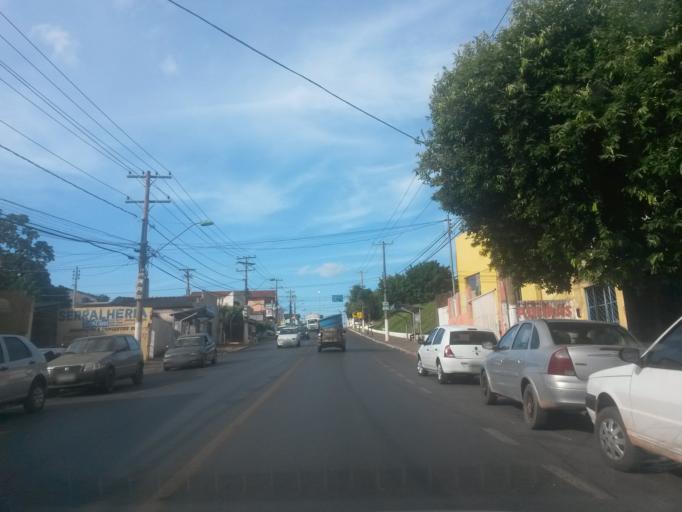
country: BR
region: Mato Grosso
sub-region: Cuiaba
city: Cuiaba
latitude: -15.5964
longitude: -56.0802
